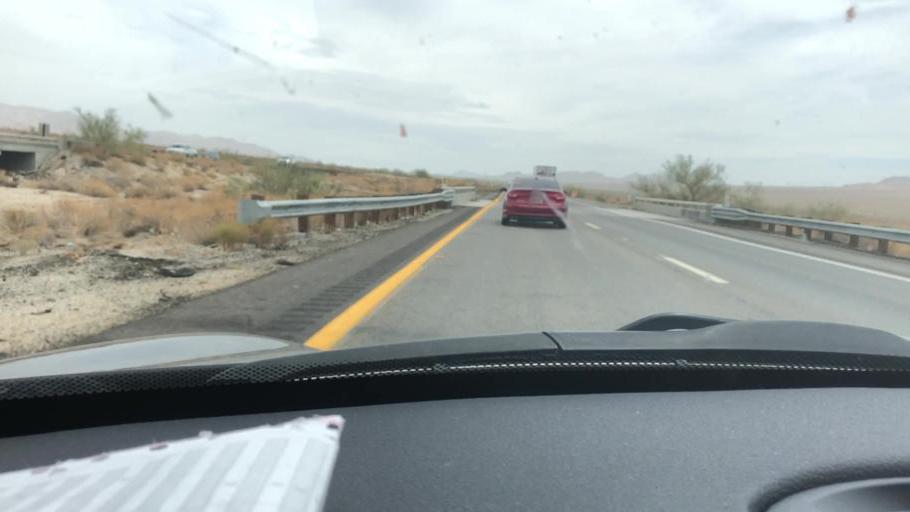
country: US
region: California
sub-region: Riverside County
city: Mecca
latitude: 33.6635
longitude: -115.8647
